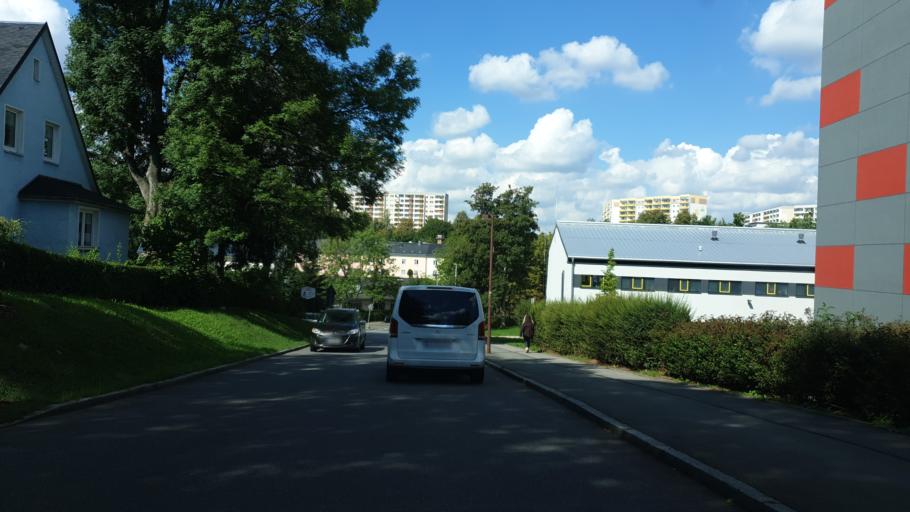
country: DE
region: Saxony
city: Neukirchen
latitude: 50.7912
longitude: 12.9023
